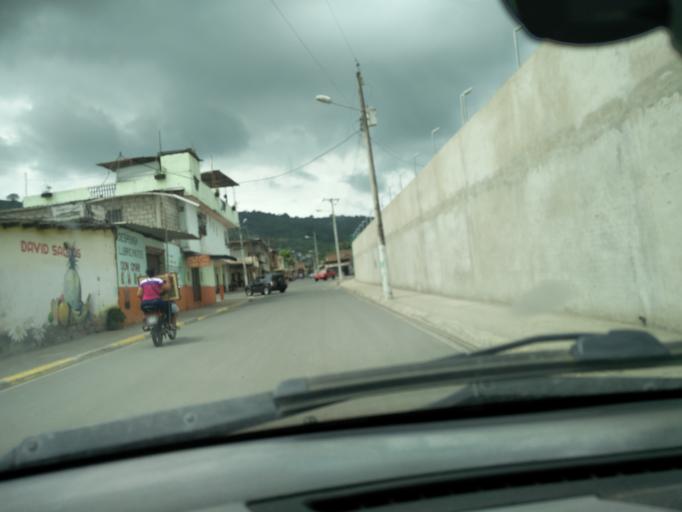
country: EC
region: Manabi
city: Portoviejo
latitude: -1.0529
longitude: -80.4484
